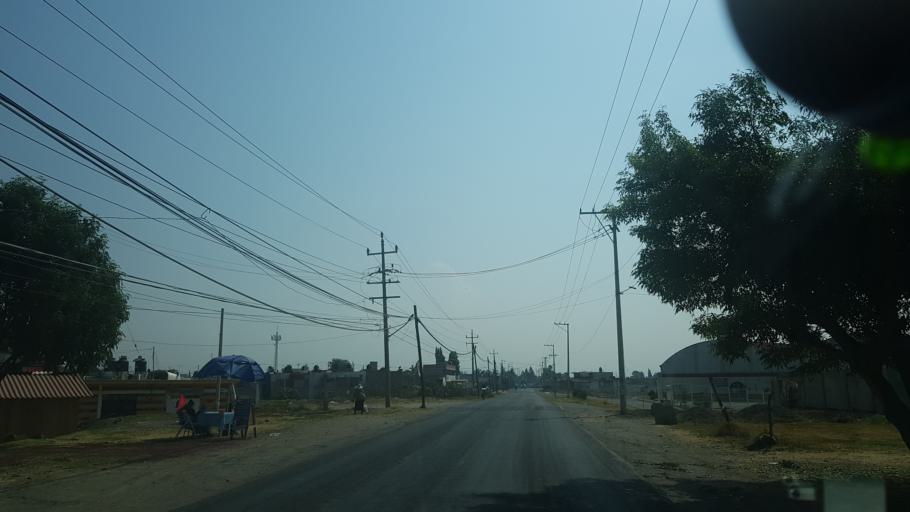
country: MX
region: Puebla
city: Cholula
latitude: 19.0572
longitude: -98.3226
